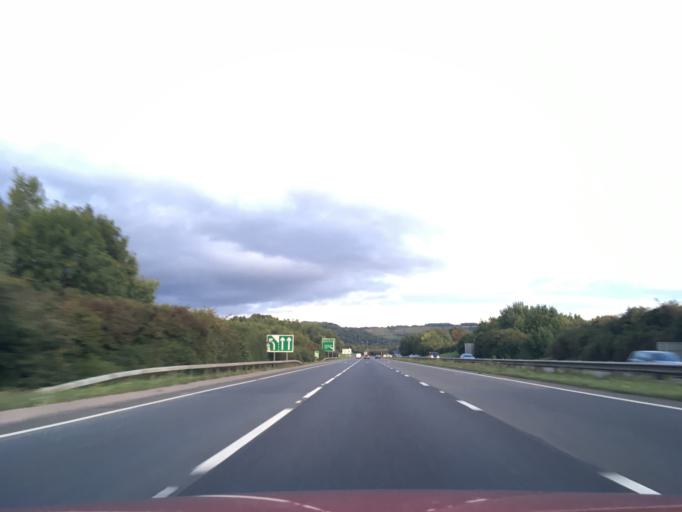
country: GB
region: England
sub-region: Gloucestershire
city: Shurdington
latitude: 51.8531
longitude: -2.1504
